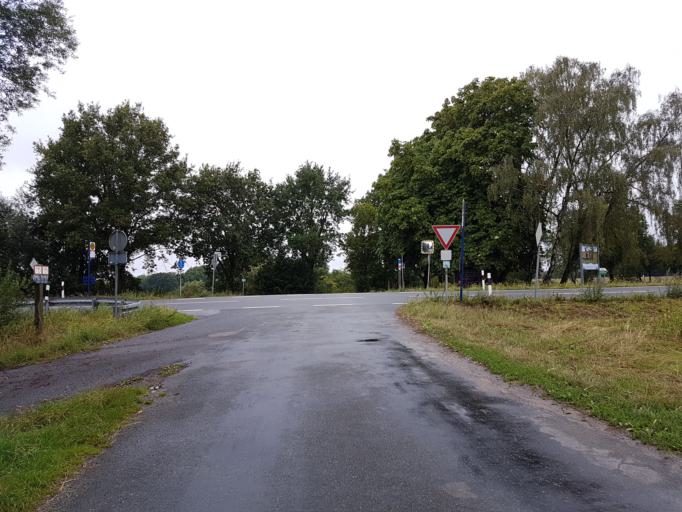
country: DE
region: North Rhine-Westphalia
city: Olfen
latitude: 51.7193
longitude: 7.3867
